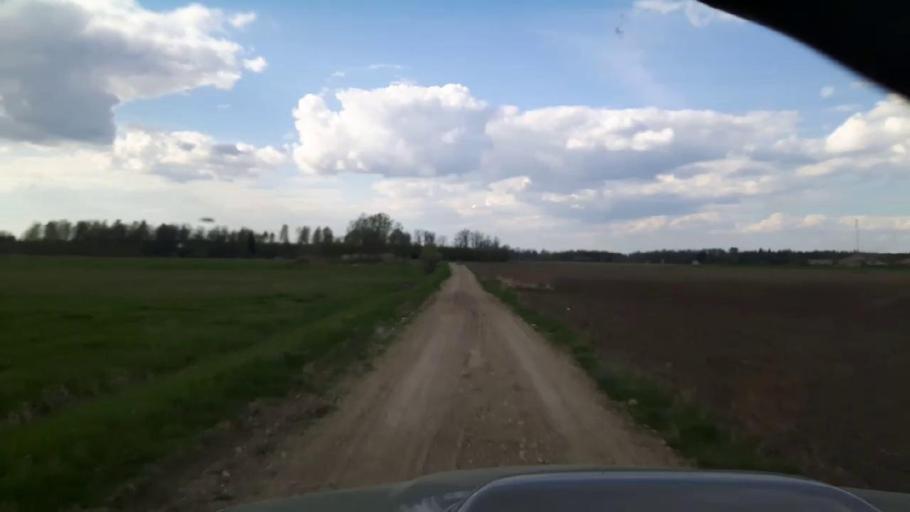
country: EE
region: Paernumaa
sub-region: Sindi linn
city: Sindi
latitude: 58.4373
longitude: 24.7670
